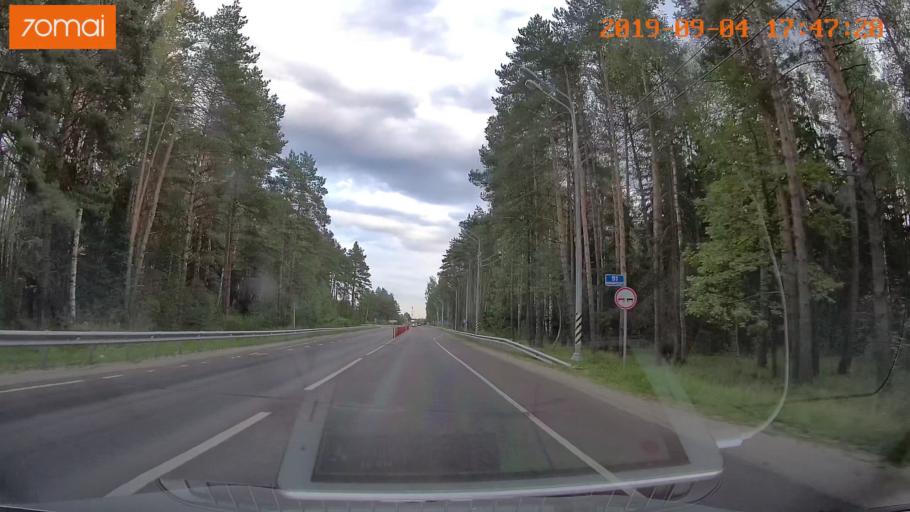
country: RU
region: Moskovskaya
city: Imeni Tsyurupy
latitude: 55.5462
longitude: 38.6407
